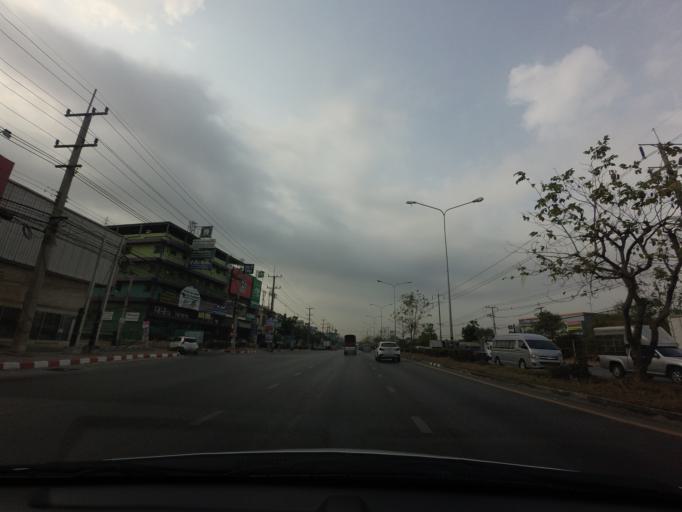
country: TH
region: Bangkok
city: Thawi Watthana
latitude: 13.7654
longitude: 100.3286
